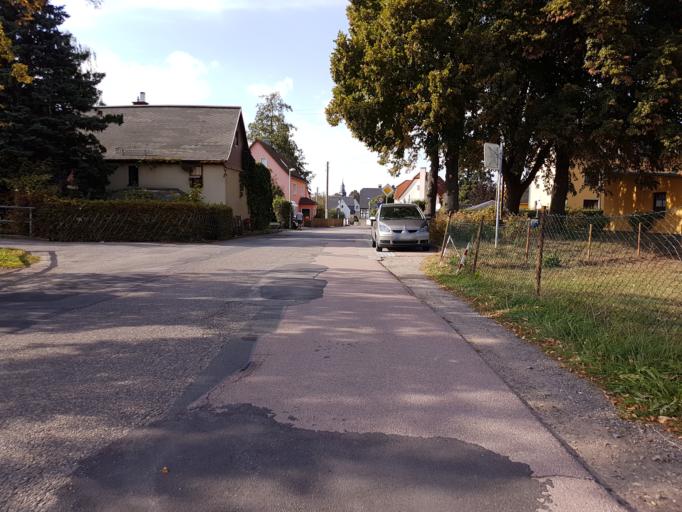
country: DE
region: Saxony
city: Claussnitz
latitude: 50.9698
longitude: 12.8839
